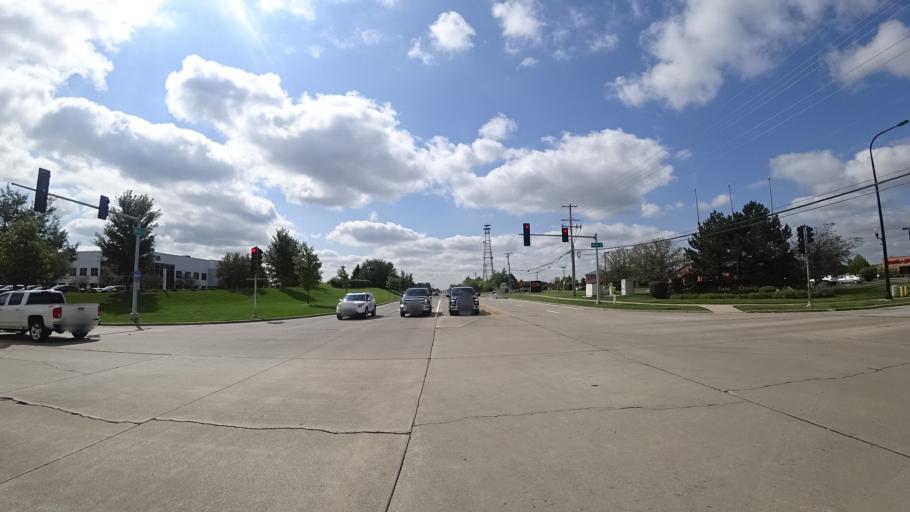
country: US
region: Illinois
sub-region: Cook County
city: Tinley Park
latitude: 41.5584
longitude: -87.8121
